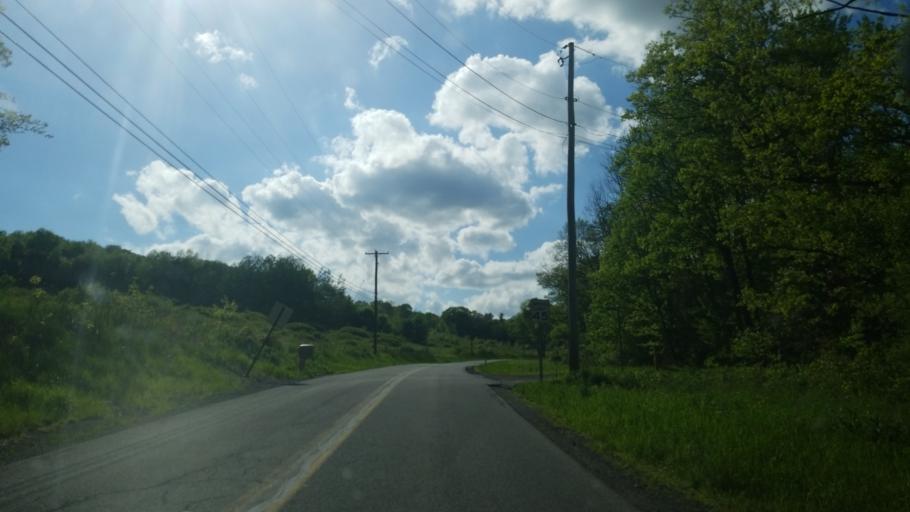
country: US
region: Pennsylvania
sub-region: Clearfield County
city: Troy
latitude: 40.9317
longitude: -78.2999
